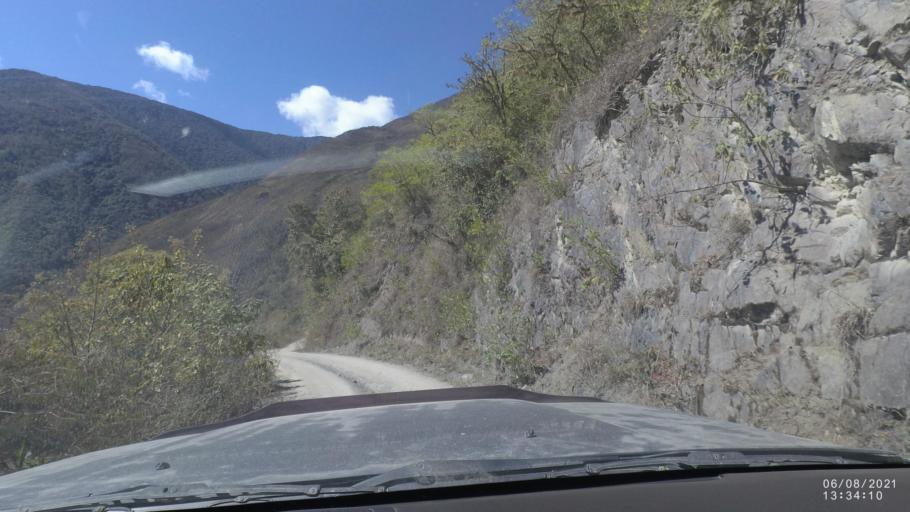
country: BO
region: La Paz
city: Quime
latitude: -16.6960
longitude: -66.7240
